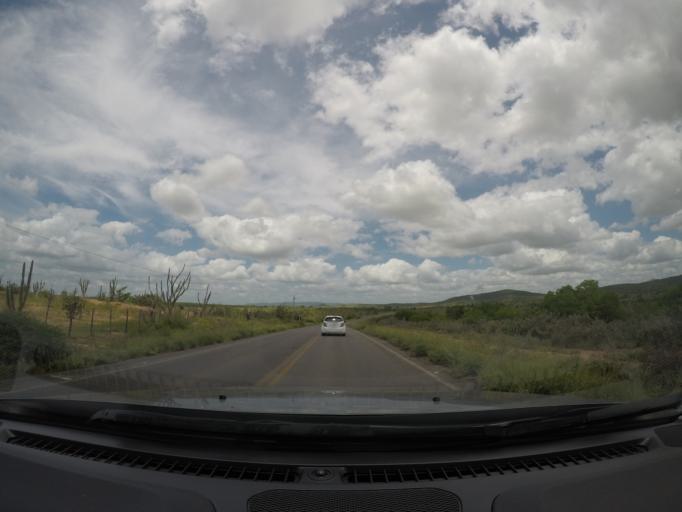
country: BR
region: Bahia
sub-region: Ipira
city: Ipira
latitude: -12.2719
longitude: -39.8480
